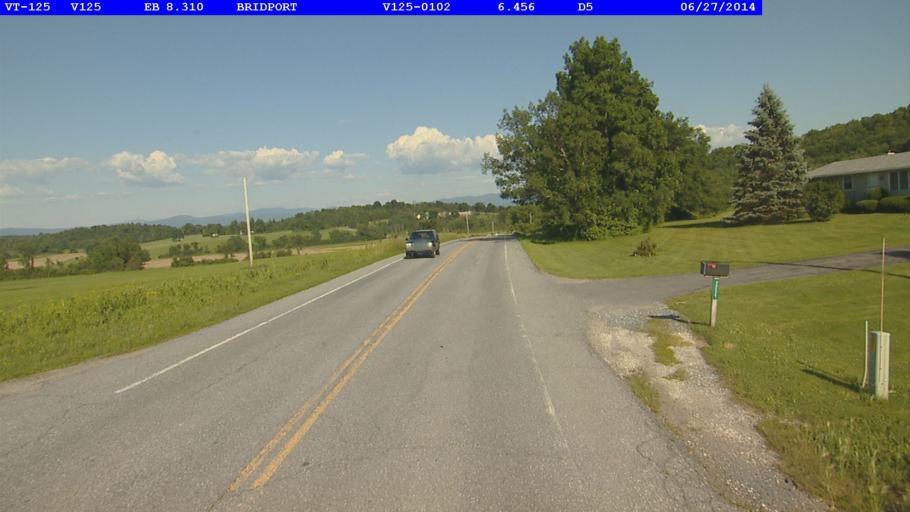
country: US
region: Vermont
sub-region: Addison County
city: Middlebury (village)
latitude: 43.9907
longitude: -73.2886
